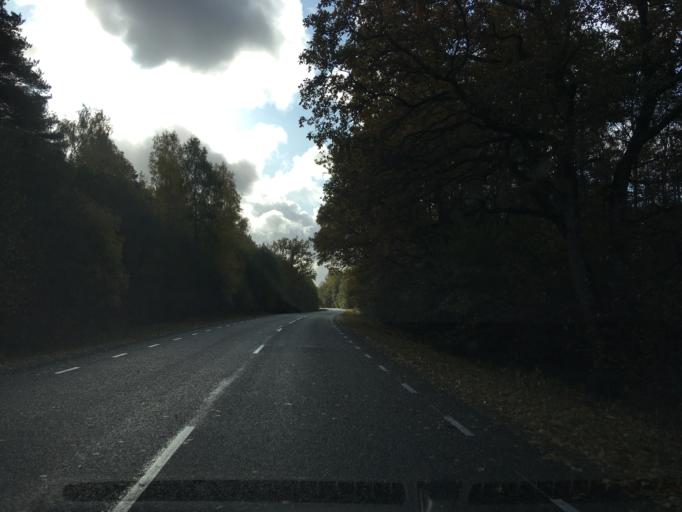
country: EE
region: Laeaene
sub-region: Lihula vald
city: Lihula
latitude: 58.6107
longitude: 23.6954
